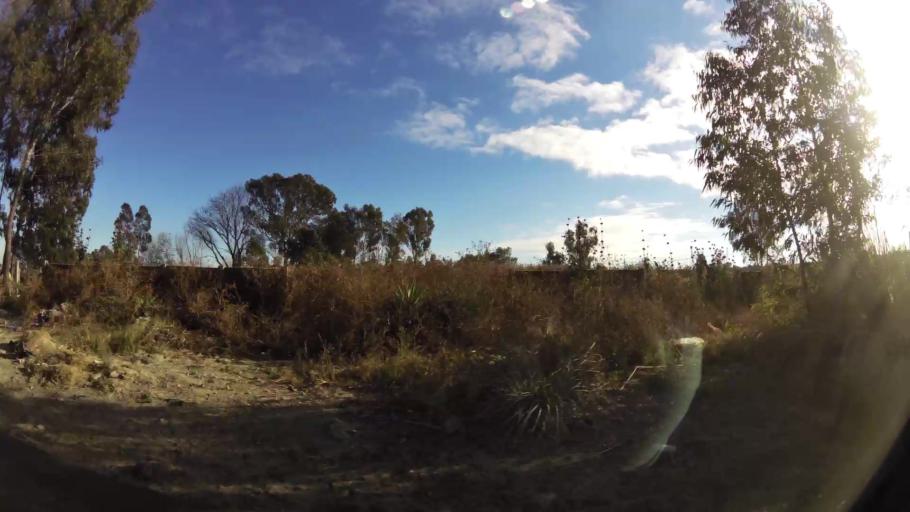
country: ZA
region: Gauteng
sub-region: City of Johannesburg Metropolitan Municipality
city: Modderfontein
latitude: -26.0397
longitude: 28.1677
